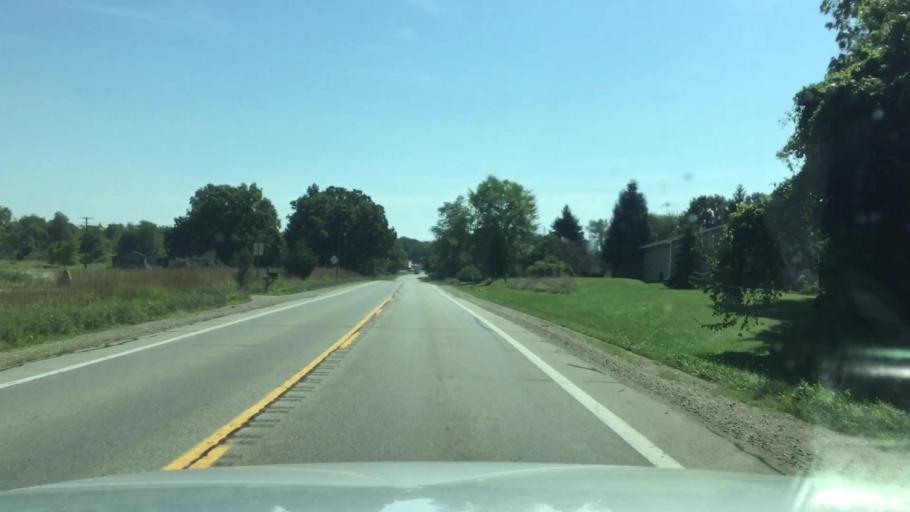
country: US
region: Michigan
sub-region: Lenawee County
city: Manitou Beach-Devils Lake
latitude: 42.0095
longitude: -84.3004
